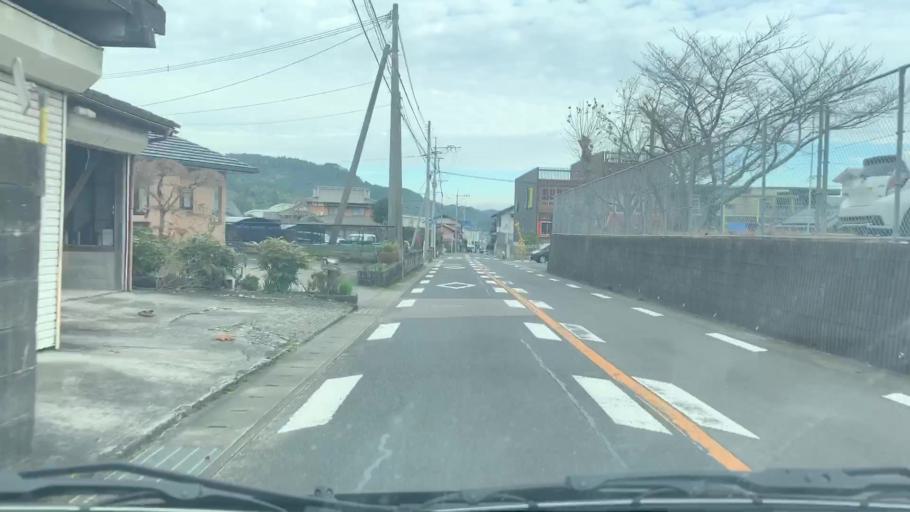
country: JP
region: Saga Prefecture
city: Takeocho-takeo
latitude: 33.1939
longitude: 129.9634
